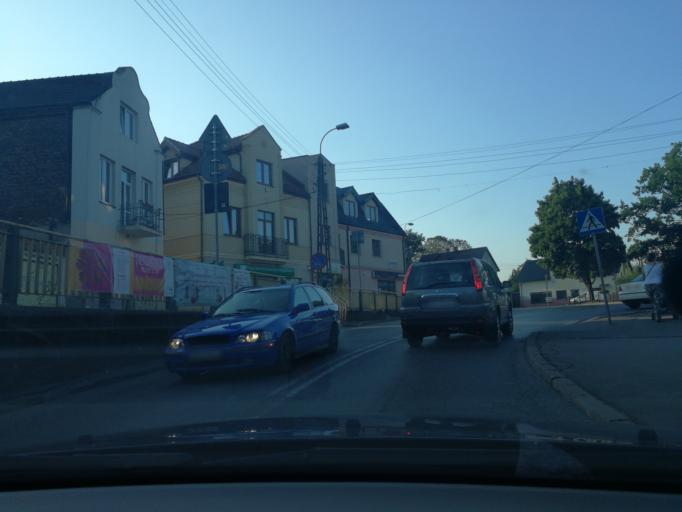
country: PL
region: Masovian Voivodeship
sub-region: Powiat pruszkowski
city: Brwinow
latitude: 52.1421
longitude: 20.7170
